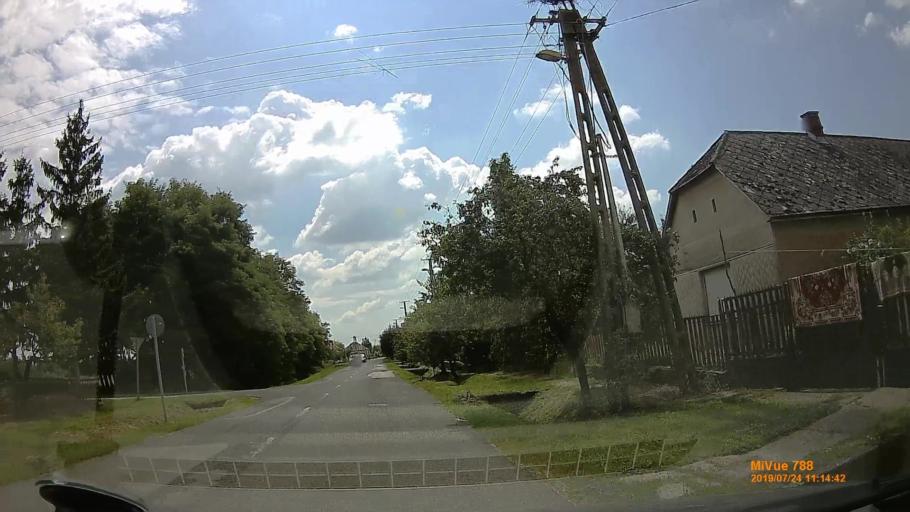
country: HU
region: Szabolcs-Szatmar-Bereg
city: Tarpa
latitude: 48.1965
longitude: 22.4511
